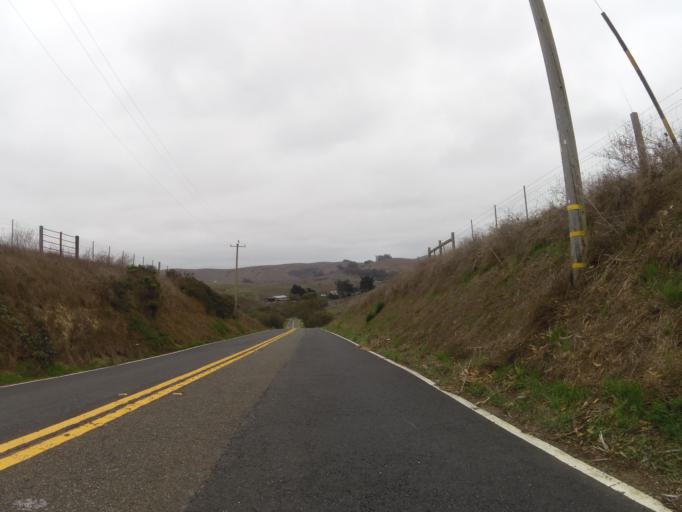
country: US
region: California
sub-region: Sonoma County
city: Occidental
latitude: 38.2800
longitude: -122.9004
